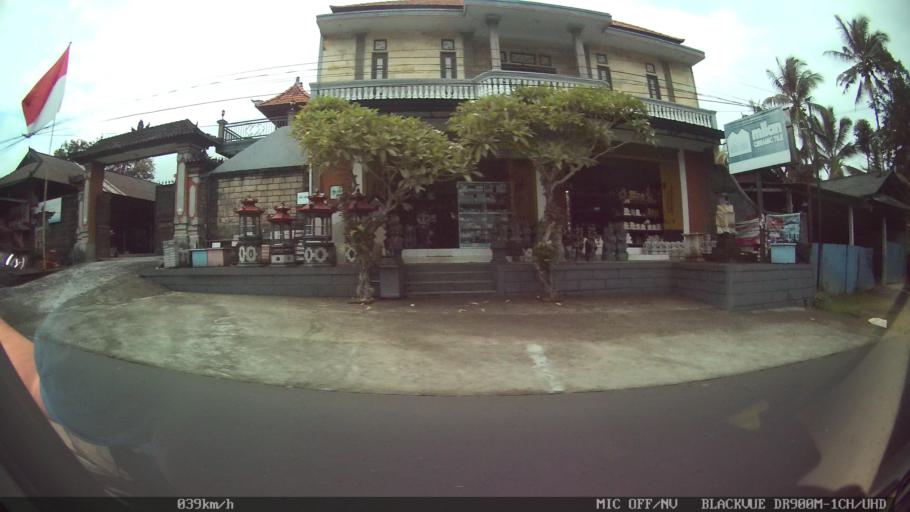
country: ID
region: Bali
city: Banjar Bebalang
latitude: -8.4869
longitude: 115.3498
